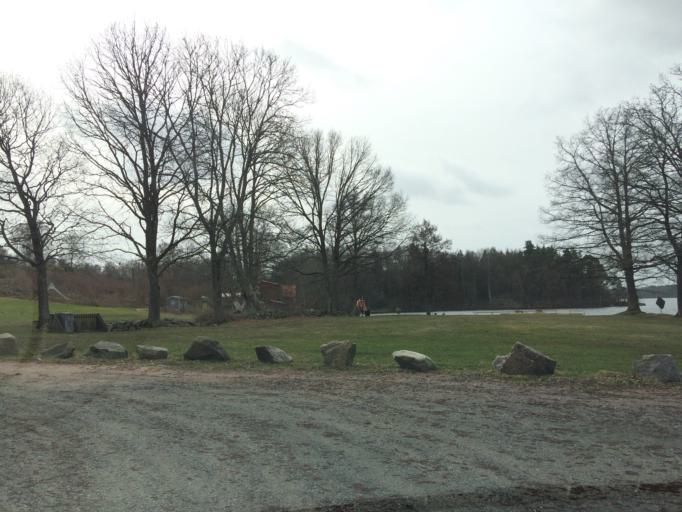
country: SE
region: Skane
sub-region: Ostra Goinge Kommun
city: Sibbhult
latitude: 56.2776
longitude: 14.3044
